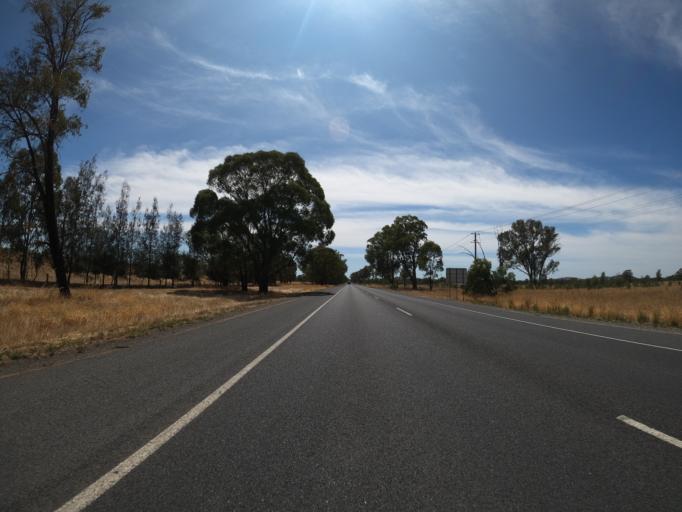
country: AU
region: Victoria
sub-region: Benalla
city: Benalla
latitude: -36.5277
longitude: 146.0468
